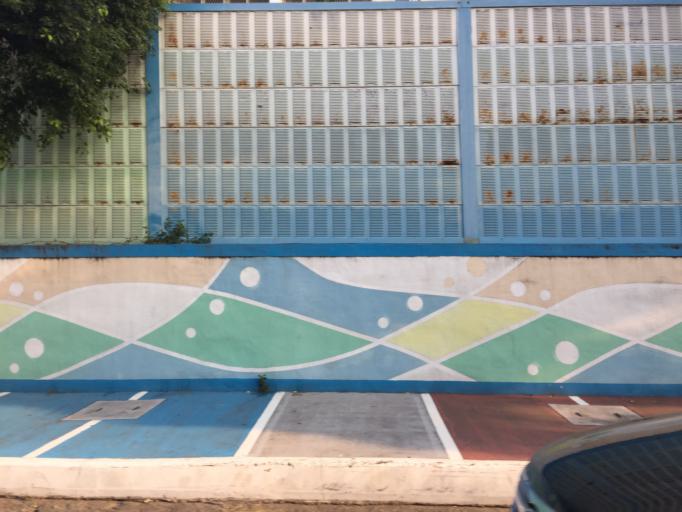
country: TW
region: Taiwan
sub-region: Hsinchu
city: Hsinchu
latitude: 24.8086
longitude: 120.9593
